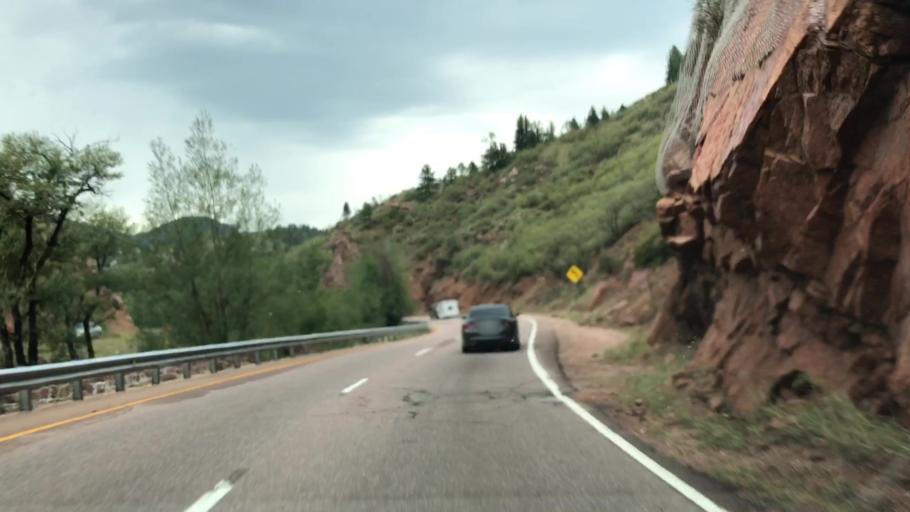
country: US
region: Colorado
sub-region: El Paso County
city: Manitou Springs
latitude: 38.8791
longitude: -104.9456
